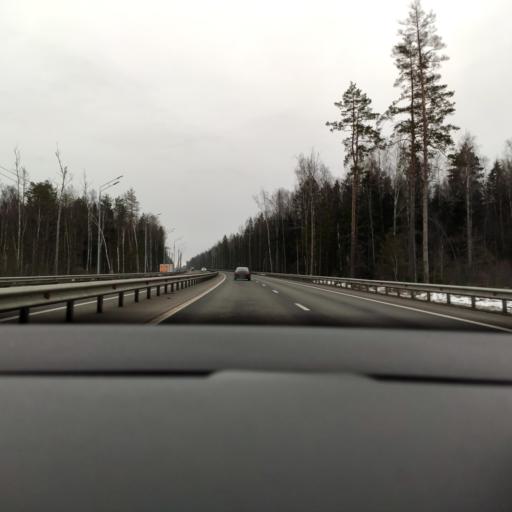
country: RU
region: Moskovskaya
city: Zvenigorod
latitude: 55.6745
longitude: 36.9057
